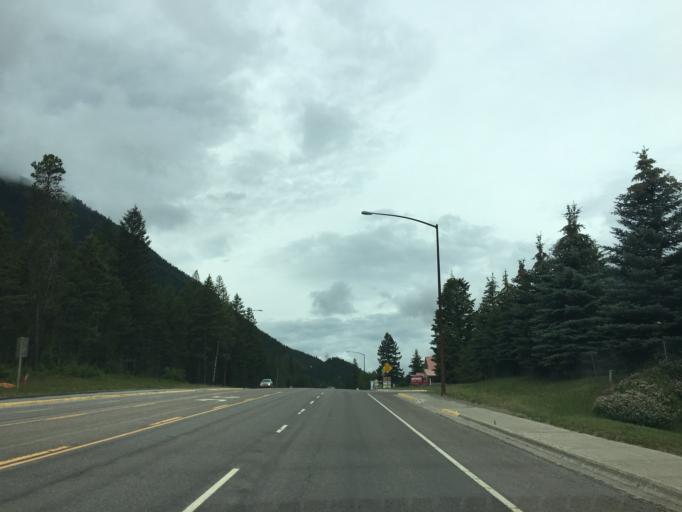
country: US
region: Montana
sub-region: Flathead County
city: Columbia Falls
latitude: 48.3857
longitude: -114.0675
